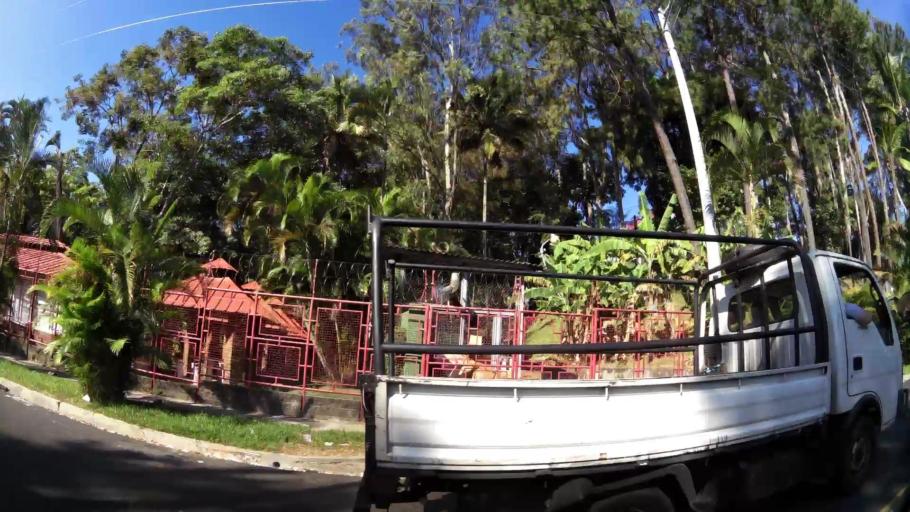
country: SV
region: La Libertad
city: Santa Tecla
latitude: 13.6752
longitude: -89.2761
